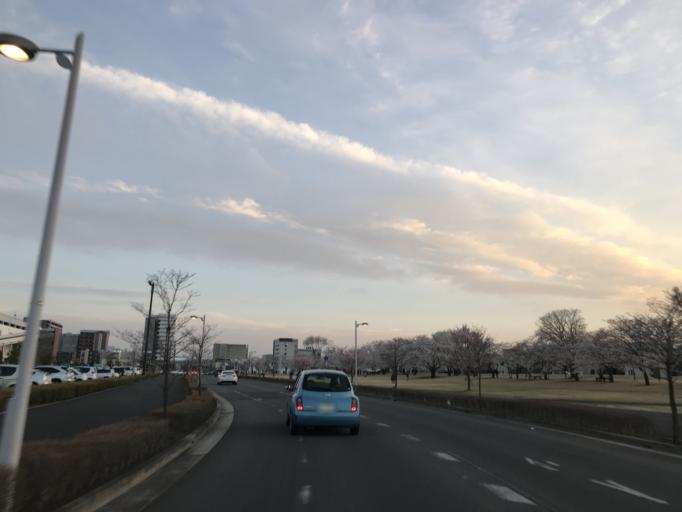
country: JP
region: Ibaraki
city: Naka
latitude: 36.0880
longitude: 140.0826
